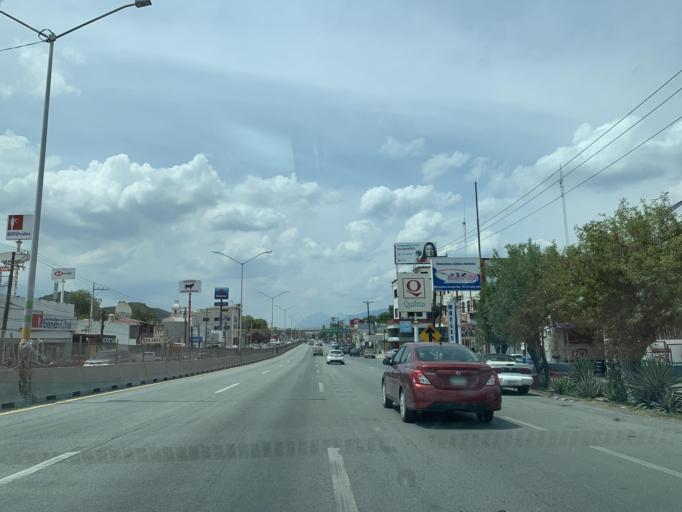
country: MX
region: Nuevo Leon
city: Santiago
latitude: 25.4024
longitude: -100.1324
